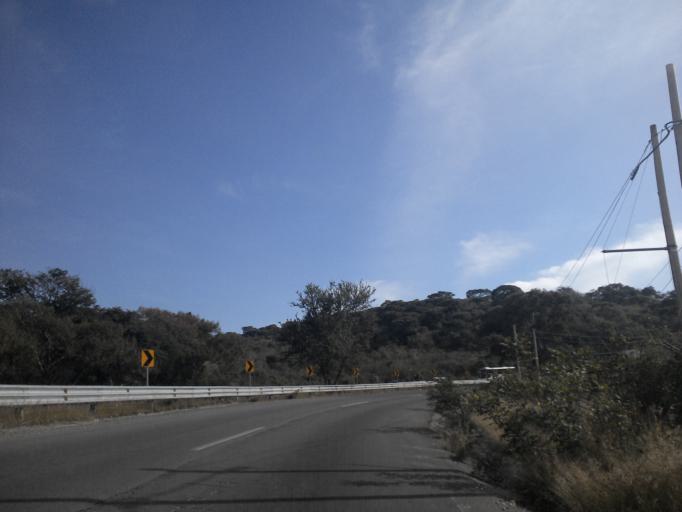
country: MX
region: Jalisco
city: Ixtlahuacan de los Membrillos
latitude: 20.3406
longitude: -103.1859
